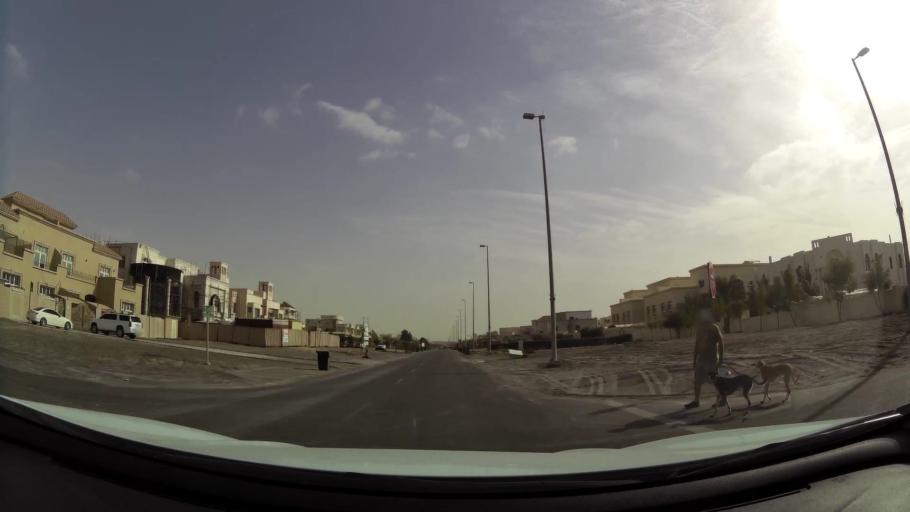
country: AE
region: Abu Dhabi
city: Abu Dhabi
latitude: 24.4147
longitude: 54.5770
